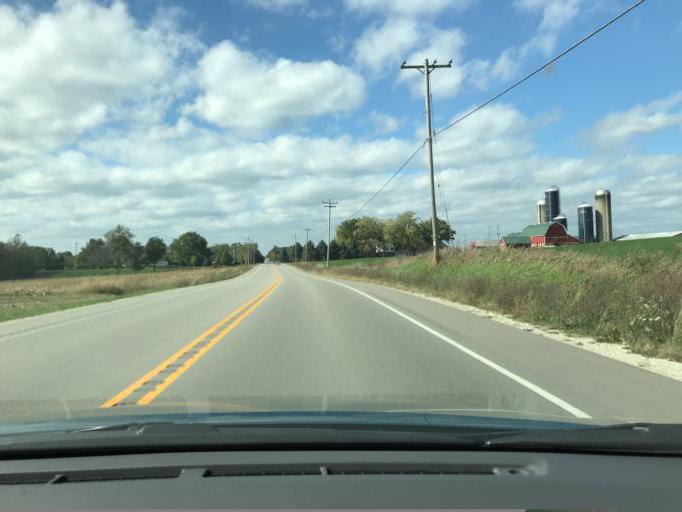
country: US
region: Wisconsin
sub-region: Racine County
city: Browns Lake
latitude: 42.6490
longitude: -88.2015
